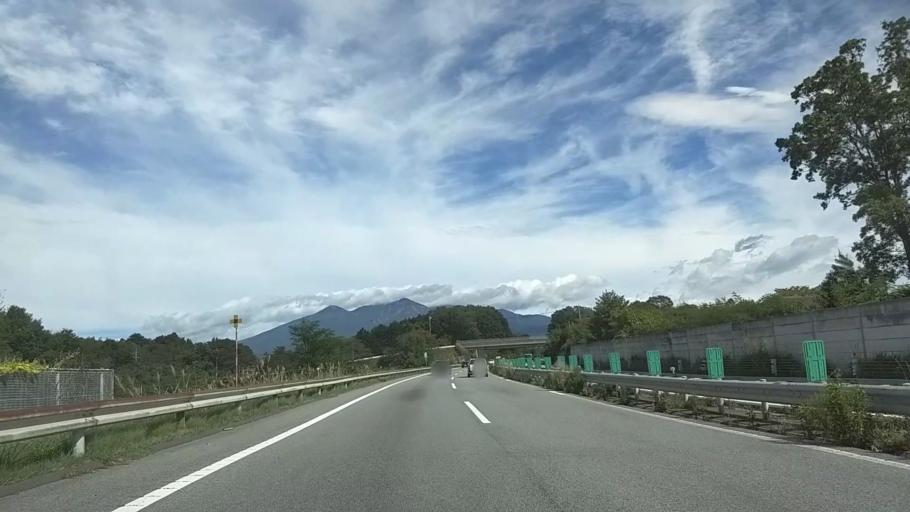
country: JP
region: Yamanashi
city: Nirasaki
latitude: 35.7979
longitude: 138.3954
